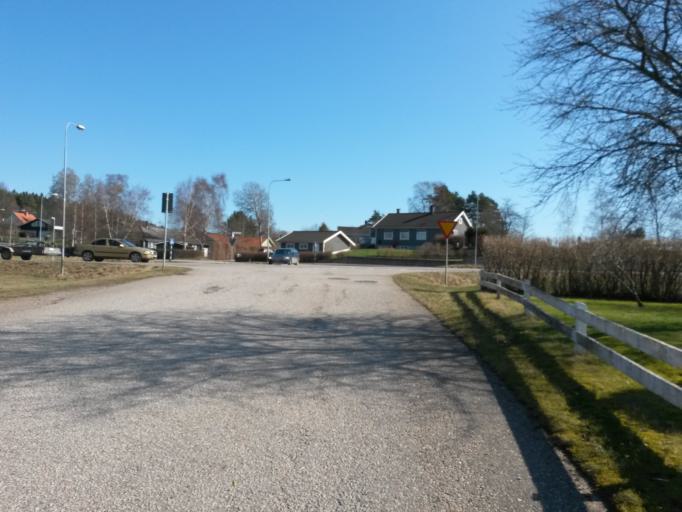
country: SE
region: Vaestra Goetaland
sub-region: Vargarda Kommun
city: Vargarda
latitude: 58.0246
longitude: 12.7996
